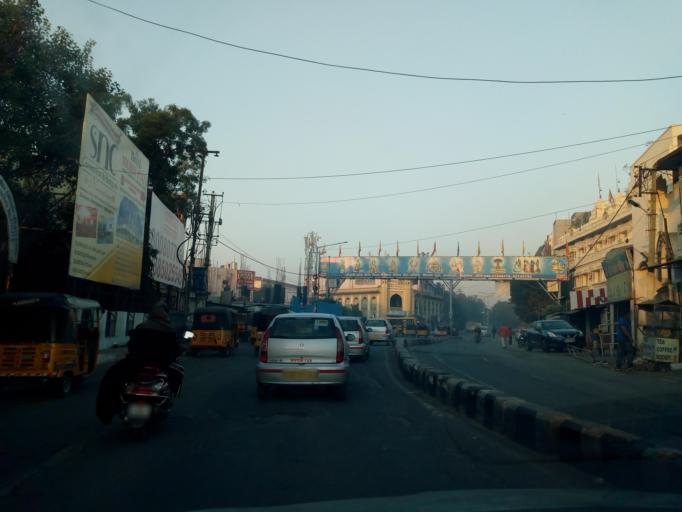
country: IN
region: Telangana
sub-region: Rangareddi
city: Gaddi Annaram
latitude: 17.3894
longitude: 78.4981
